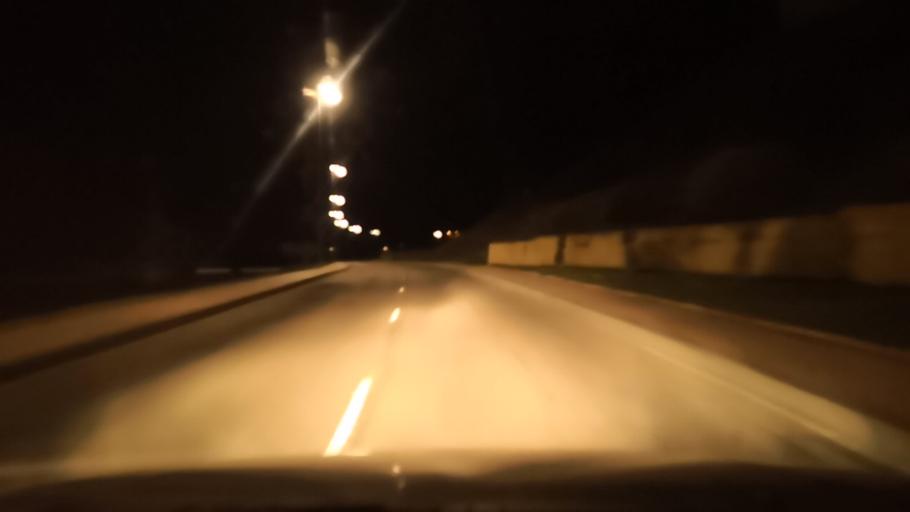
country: ES
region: Castille and Leon
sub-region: Provincia de Zamora
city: Benavente
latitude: 42.0021
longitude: -5.6847
